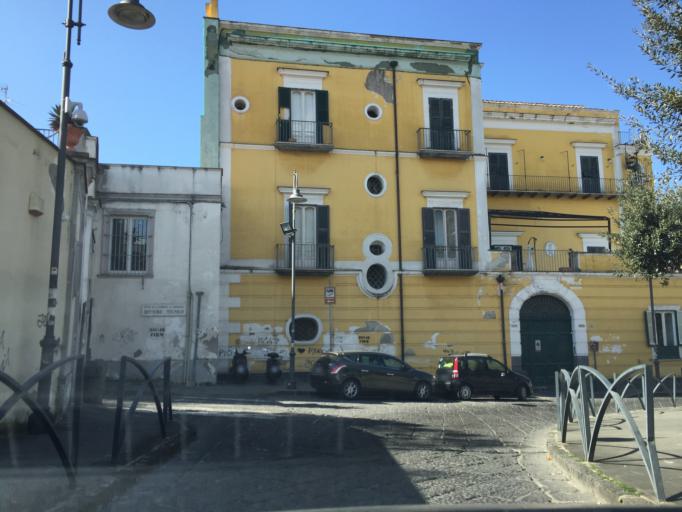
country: IT
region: Campania
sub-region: Provincia di Napoli
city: San Giorgio a Cremano
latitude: 40.8283
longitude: 14.3396
